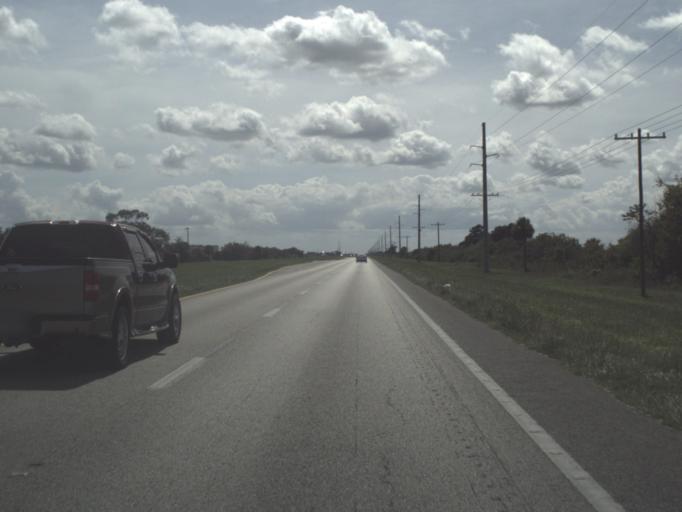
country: US
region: Florida
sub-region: Glades County
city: Moore Haven
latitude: 26.8064
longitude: -81.0827
